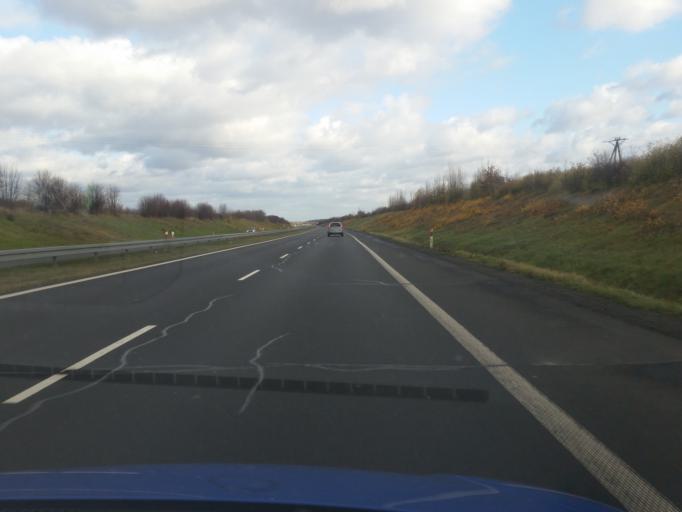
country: PL
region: Silesian Voivodeship
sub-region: Powiat czestochowski
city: Koscielec
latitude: 50.8966
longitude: 19.1913
